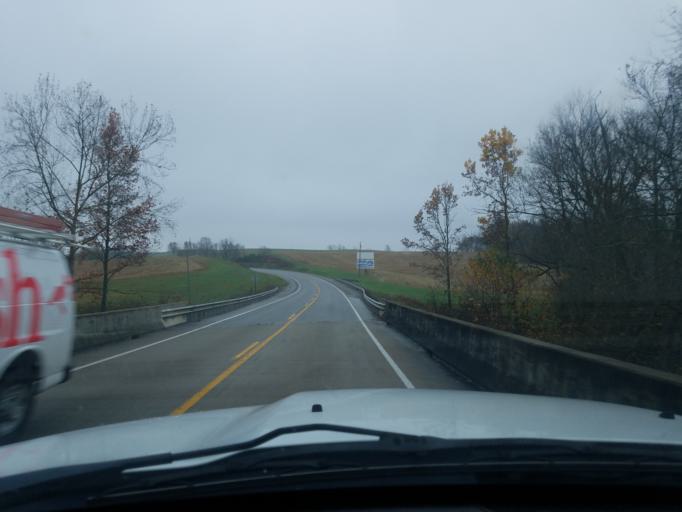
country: US
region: Kentucky
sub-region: Taylor County
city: Campbellsville
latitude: 37.3962
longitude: -85.4694
